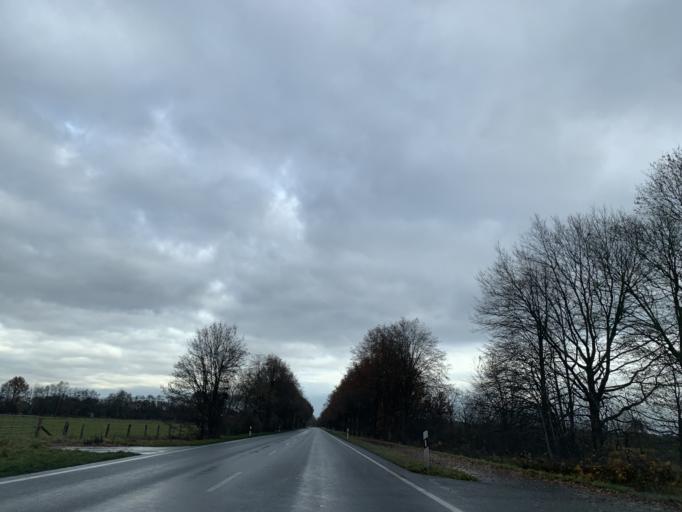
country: DE
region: North Rhine-Westphalia
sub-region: Regierungsbezirk Munster
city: Gronau
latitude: 52.1723
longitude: 6.9615
